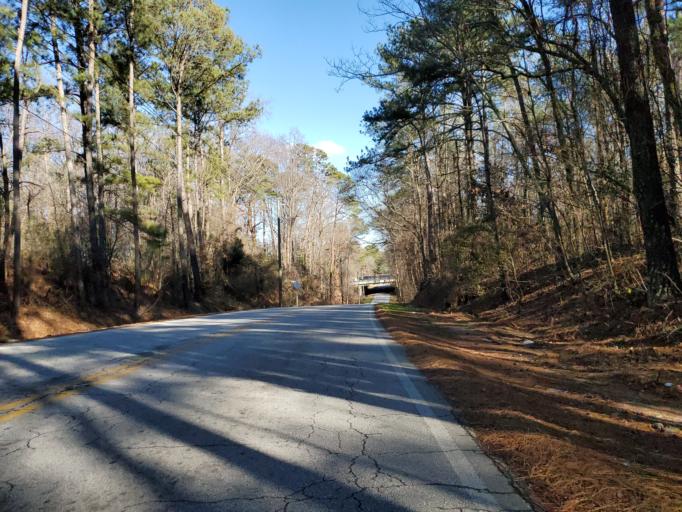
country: US
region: Georgia
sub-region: DeKalb County
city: Avondale Estates
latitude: 33.7708
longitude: -84.2362
